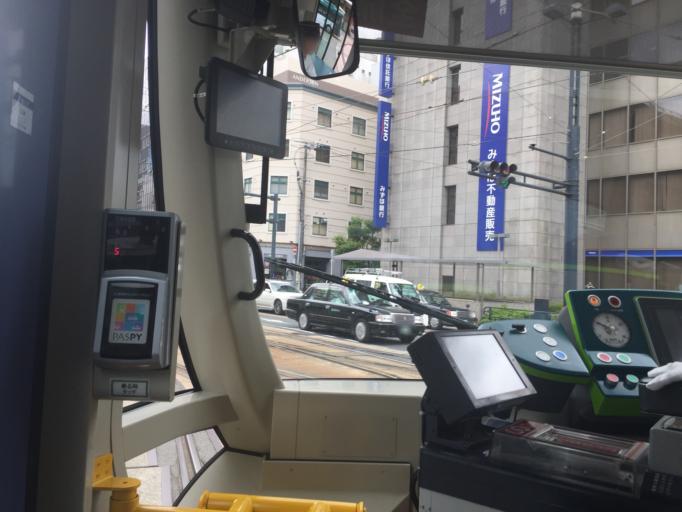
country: JP
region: Hiroshima
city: Hiroshima-shi
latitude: 34.3953
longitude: 132.4578
